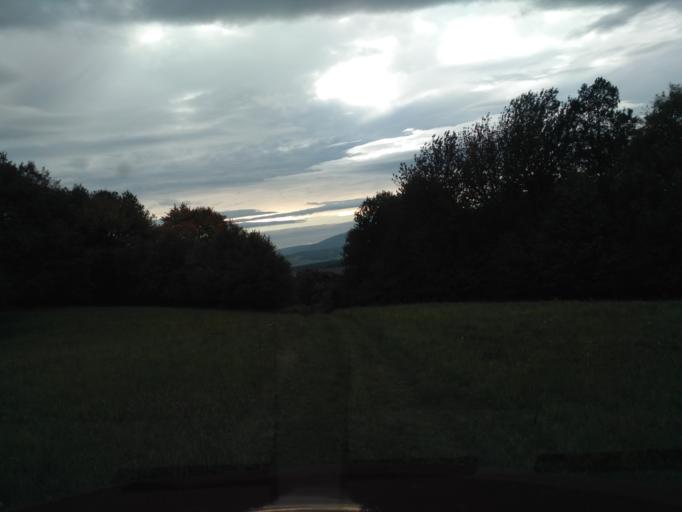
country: SK
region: Presovsky
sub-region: Okres Presov
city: Presov
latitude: 48.8949
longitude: 21.3410
